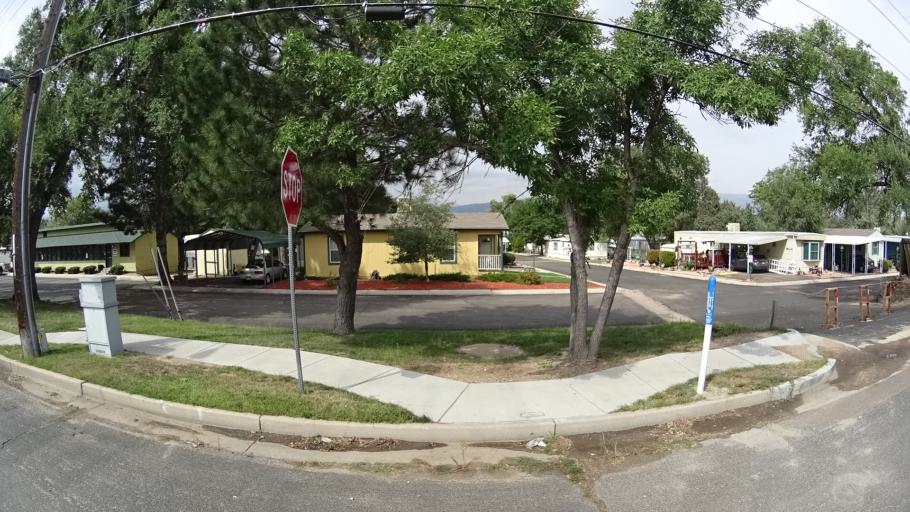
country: US
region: Colorado
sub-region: El Paso County
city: Colorado Springs
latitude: 38.8861
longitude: -104.8224
